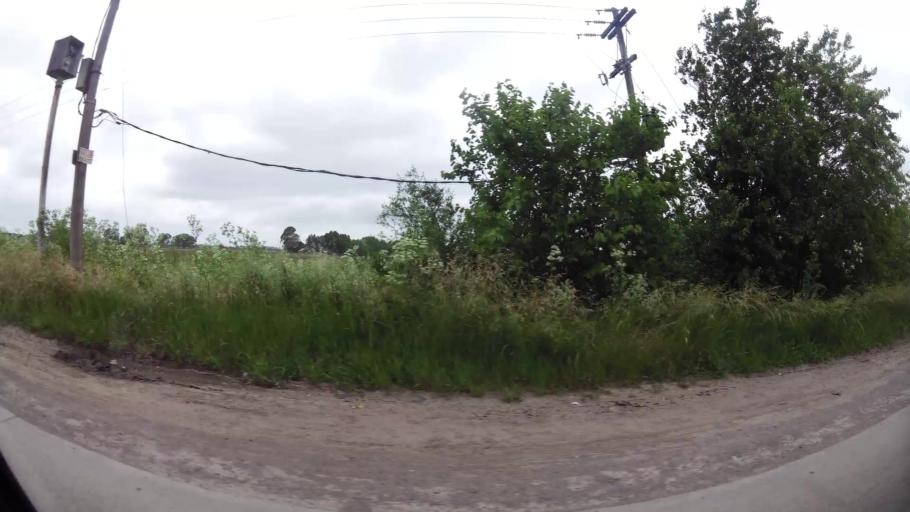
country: AR
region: Buenos Aires
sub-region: Partido de Brandsen
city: Brandsen
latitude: -35.0499
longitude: -58.1079
